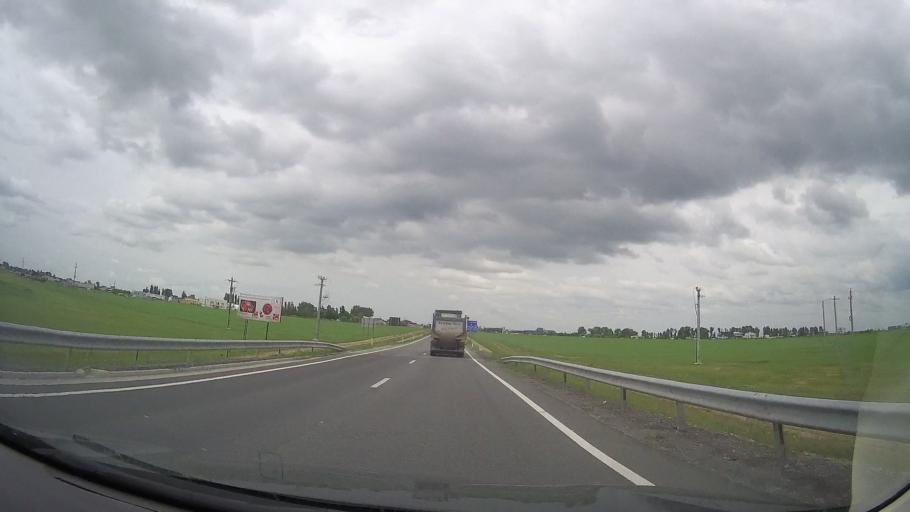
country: RO
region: Dolj
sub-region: Comuna Carcea
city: Carcea
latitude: 44.3089
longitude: 23.9133
